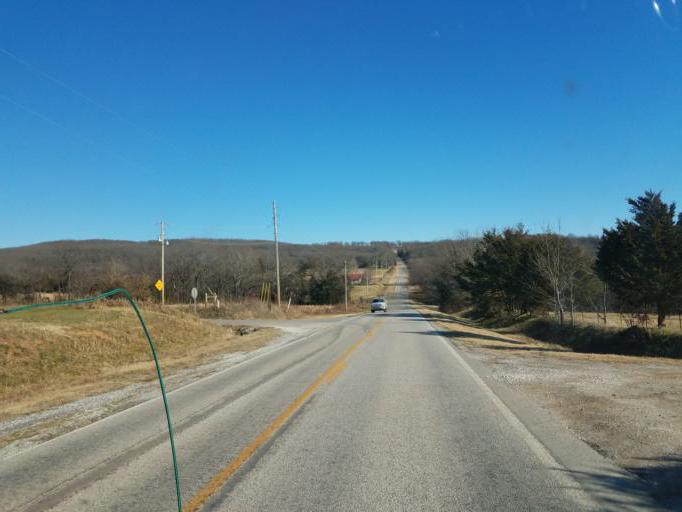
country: US
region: Arkansas
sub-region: Washington County
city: Elkins
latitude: 36.0266
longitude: -94.0086
